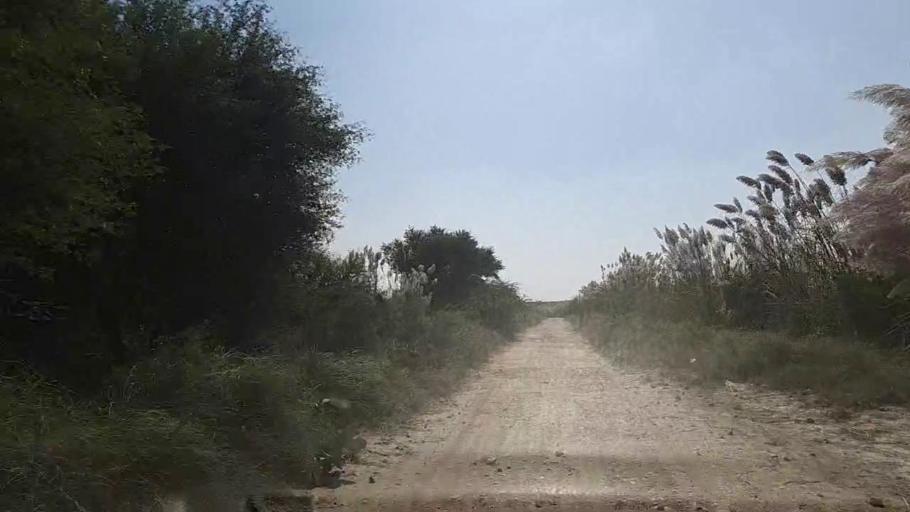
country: PK
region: Sindh
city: Daro Mehar
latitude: 24.8304
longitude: 68.0889
